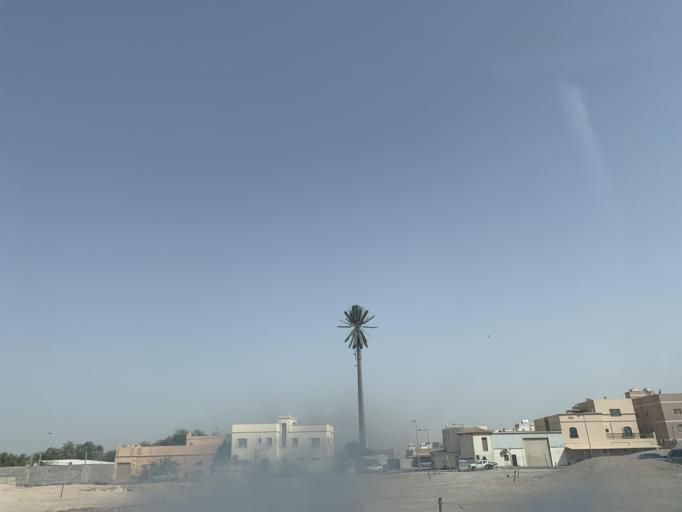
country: BH
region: Manama
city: Jidd Hafs
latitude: 26.2152
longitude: 50.5134
